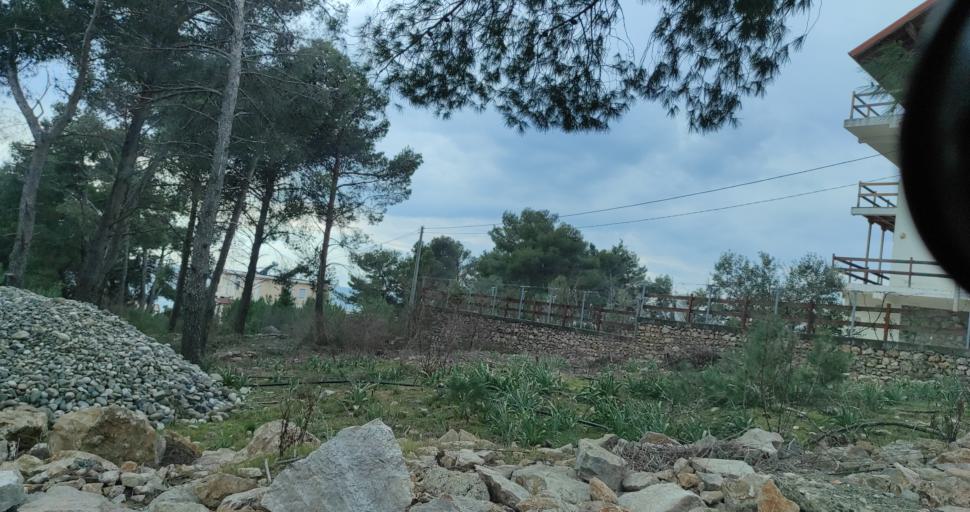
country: AL
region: Lezhe
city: Shengjin
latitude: 41.8132
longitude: 19.5821
